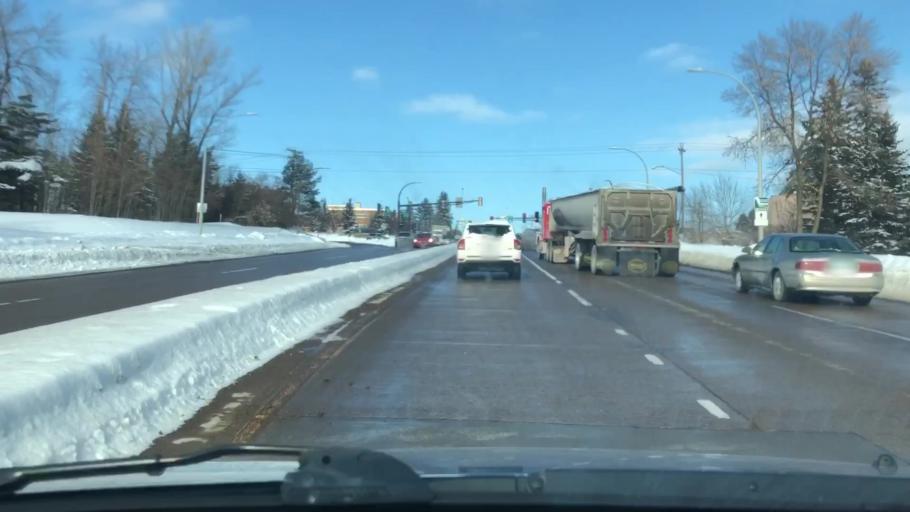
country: US
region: Minnesota
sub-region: Saint Louis County
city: Duluth
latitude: 46.7949
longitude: -92.1070
